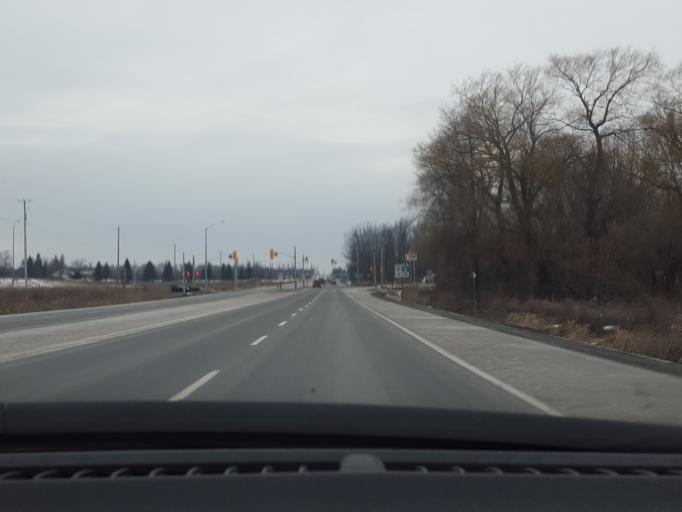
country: CA
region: Ontario
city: Keswick
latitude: 44.1897
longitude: -79.4374
